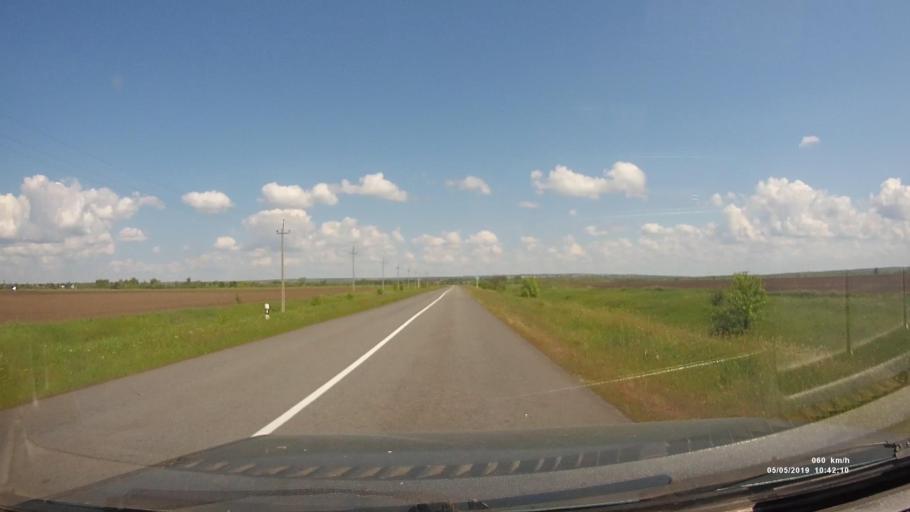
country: RU
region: Rostov
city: Ust'-Donetskiy
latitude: 47.5967
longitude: 40.8371
